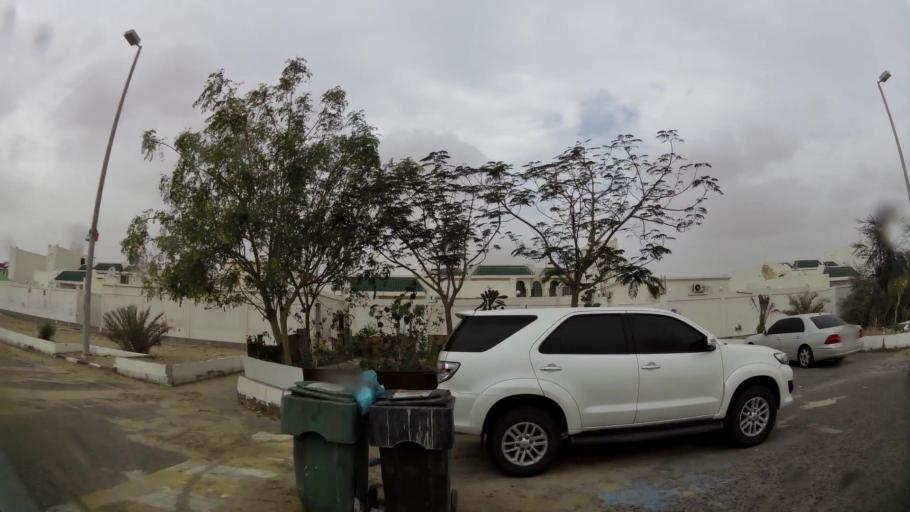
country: AE
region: Abu Dhabi
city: Abu Dhabi
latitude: 24.3621
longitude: 54.6583
